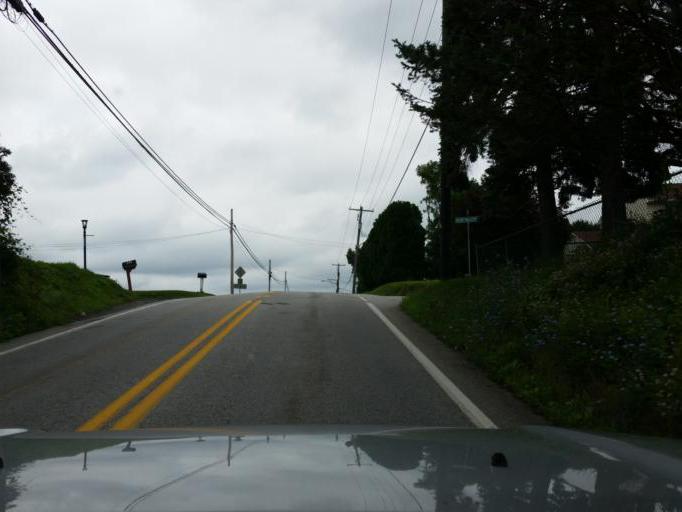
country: US
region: Pennsylvania
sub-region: Dauphin County
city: Rutherford
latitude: 40.2664
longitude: -76.7825
